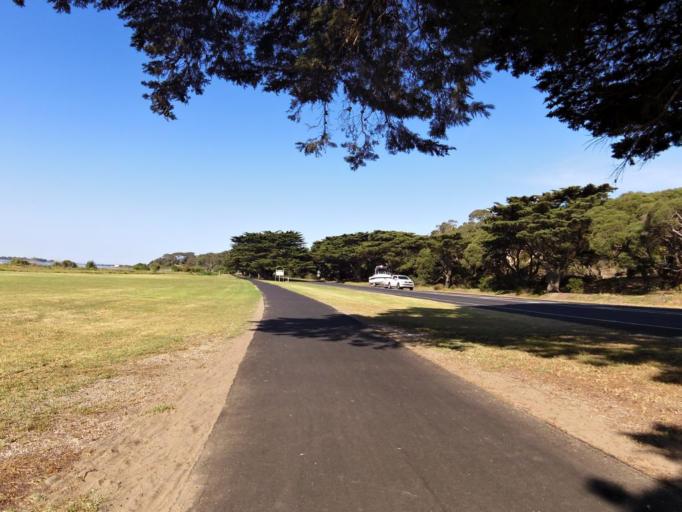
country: AU
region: Victoria
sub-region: Queenscliffe
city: Queenscliff
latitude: -38.2707
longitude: 144.6404
